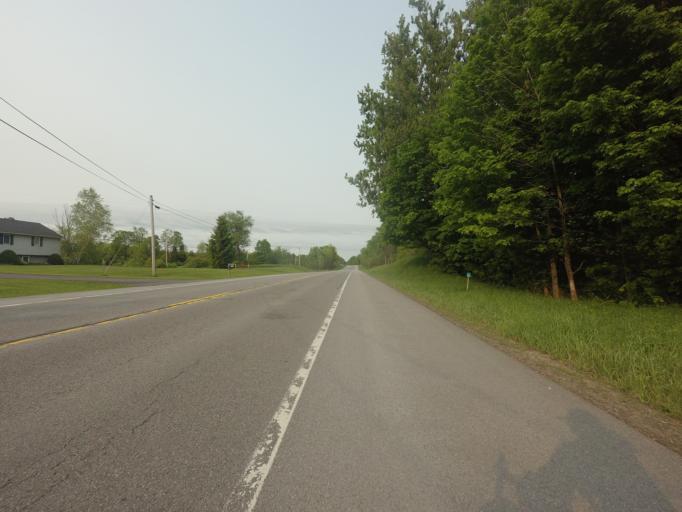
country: US
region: New York
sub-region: Jefferson County
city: Carthage
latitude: 44.0606
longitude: -75.5392
